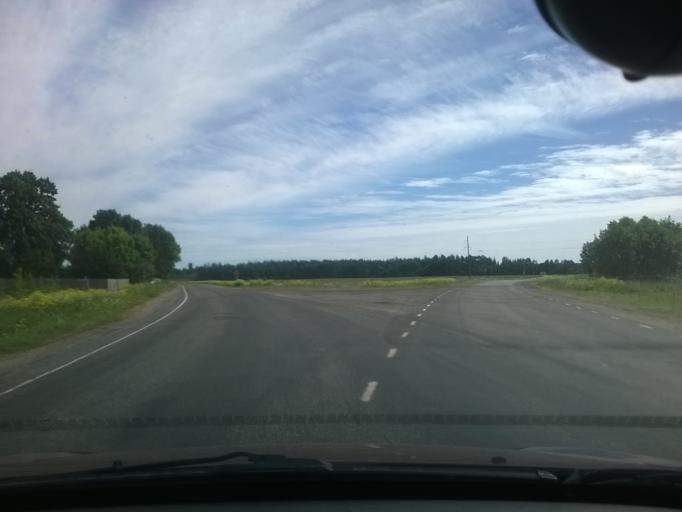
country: EE
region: Harju
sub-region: Raasiku vald
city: Raasiku
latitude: 59.2991
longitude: 25.1733
